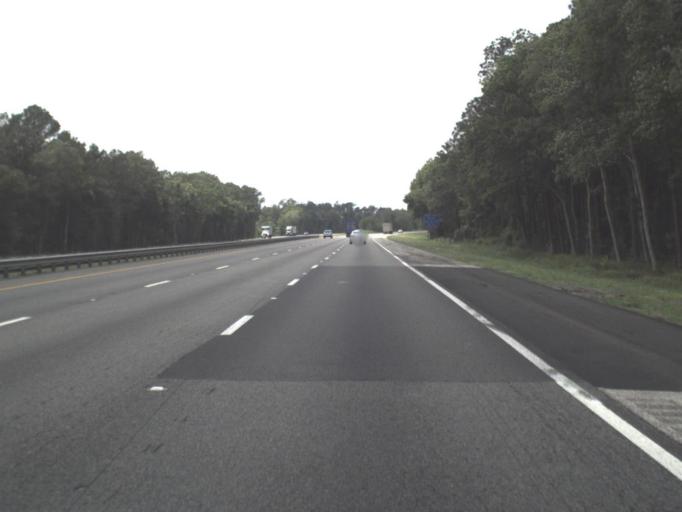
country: US
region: Florida
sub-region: Saint Johns County
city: Butler Beach
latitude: 29.6758
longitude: -81.3109
